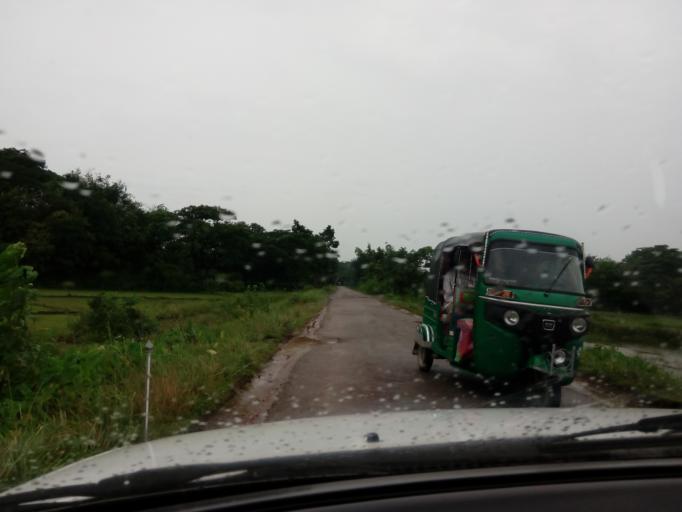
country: BD
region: Sylhet
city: Sylhet
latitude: 24.9642
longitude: 91.7940
